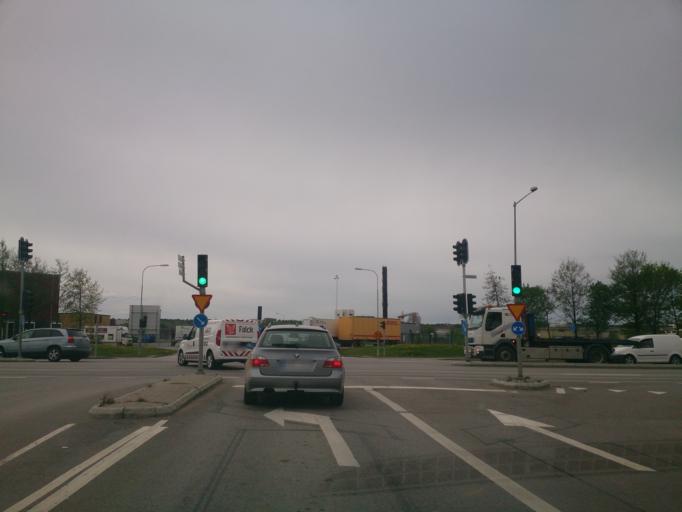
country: SE
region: OEstergoetland
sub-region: Linkopings Kommun
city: Linkoping
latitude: 58.4274
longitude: 15.6116
